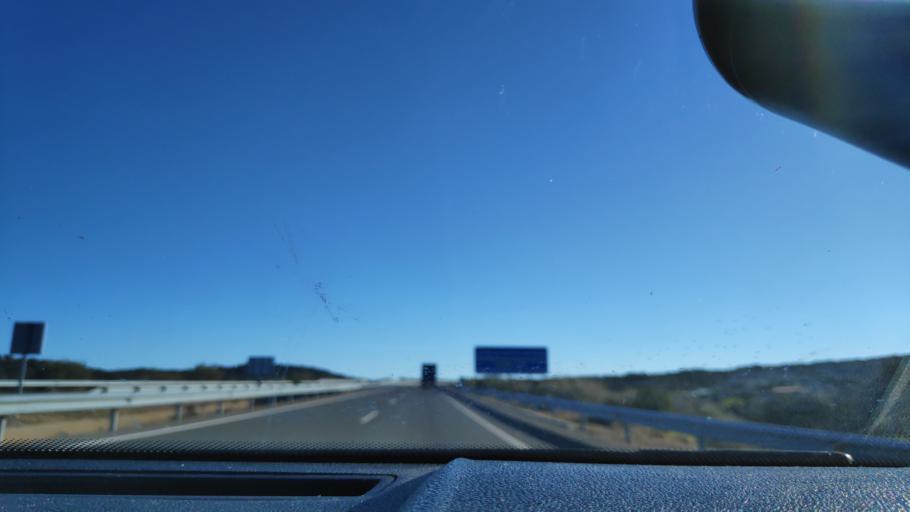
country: ES
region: Extremadura
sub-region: Provincia de Badajoz
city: Monesterio
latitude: 38.1265
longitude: -6.2714
